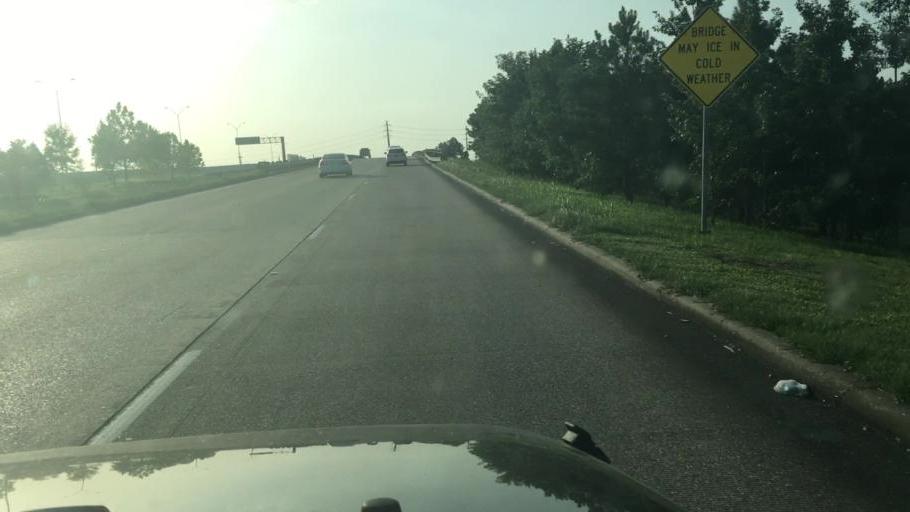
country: US
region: Texas
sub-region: Harris County
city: Atascocita
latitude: 29.9305
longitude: -95.2037
